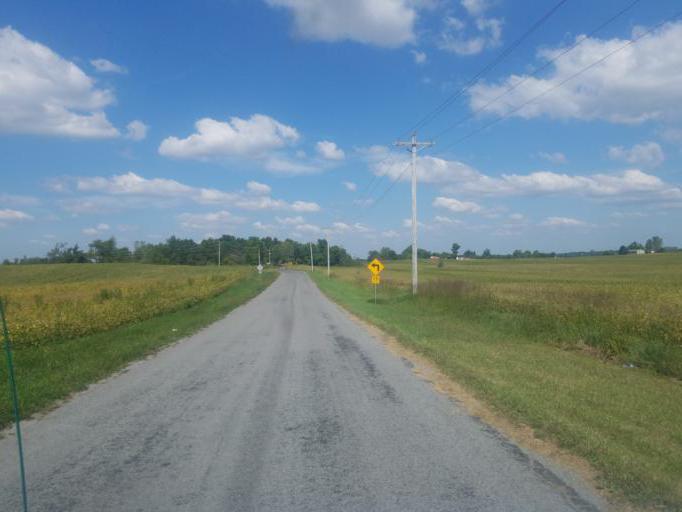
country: US
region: Ohio
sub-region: Hardin County
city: Ada
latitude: 40.6528
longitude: -83.8850
